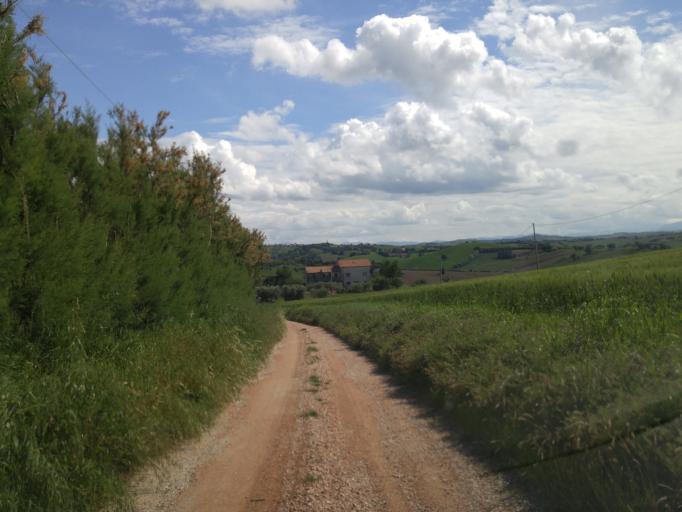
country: IT
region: The Marches
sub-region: Provincia di Pesaro e Urbino
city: San Costanzo
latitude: 43.7878
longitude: 13.0557
